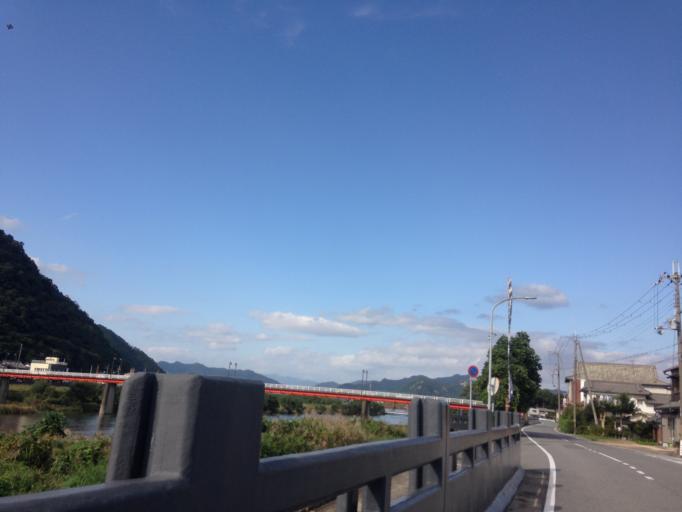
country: JP
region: Hyogo
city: Tatsunocho-tominaga
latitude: 34.8654
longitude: 134.5500
